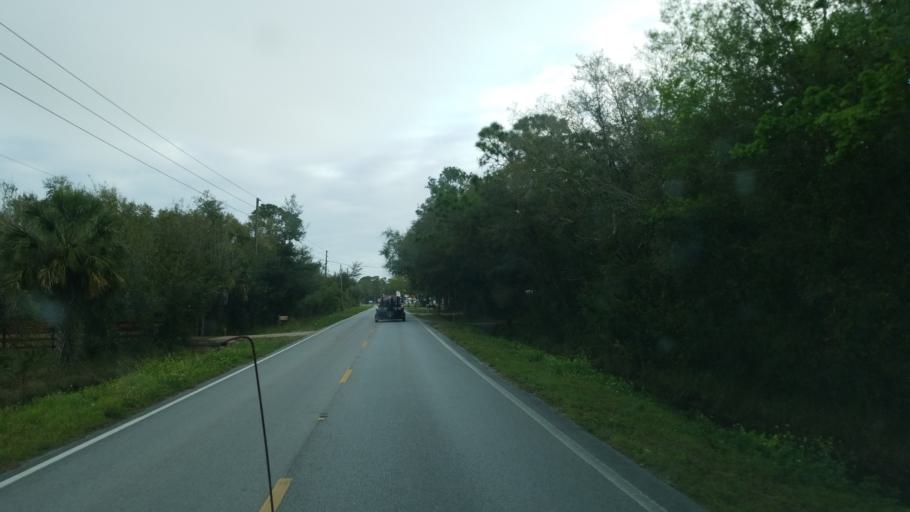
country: US
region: Florida
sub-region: Polk County
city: Babson Park
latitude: 27.9419
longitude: -81.4270
